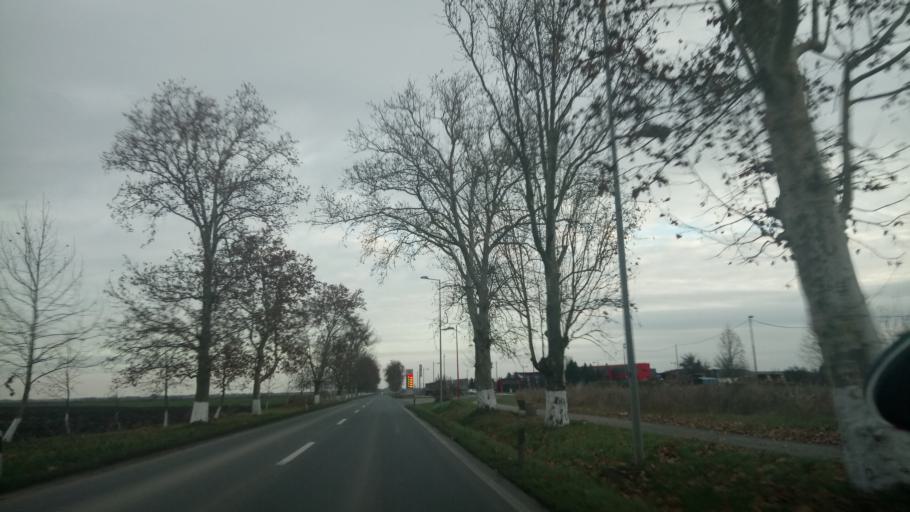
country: RS
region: Autonomna Pokrajina Vojvodina
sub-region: Sremski Okrug
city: Stara Pazova
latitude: 44.9697
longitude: 20.1790
